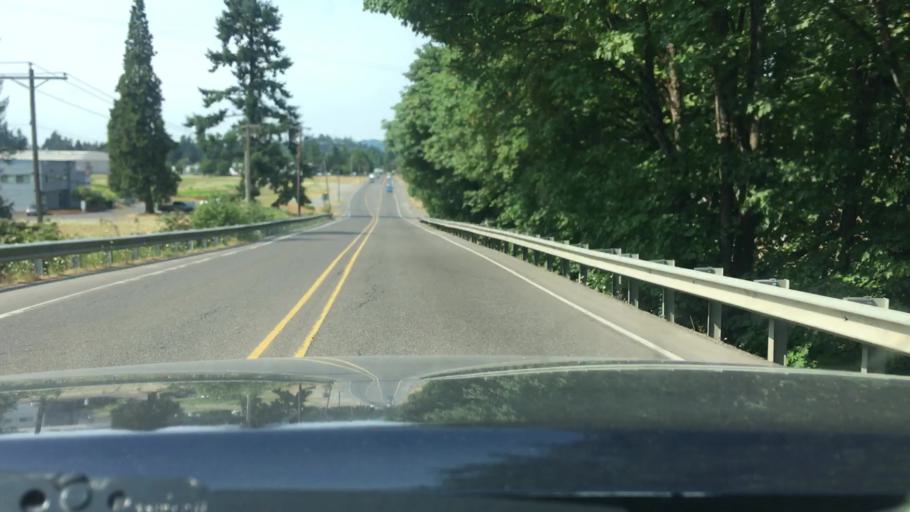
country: US
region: Oregon
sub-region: Lane County
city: Springfield
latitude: 44.0314
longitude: -123.0265
